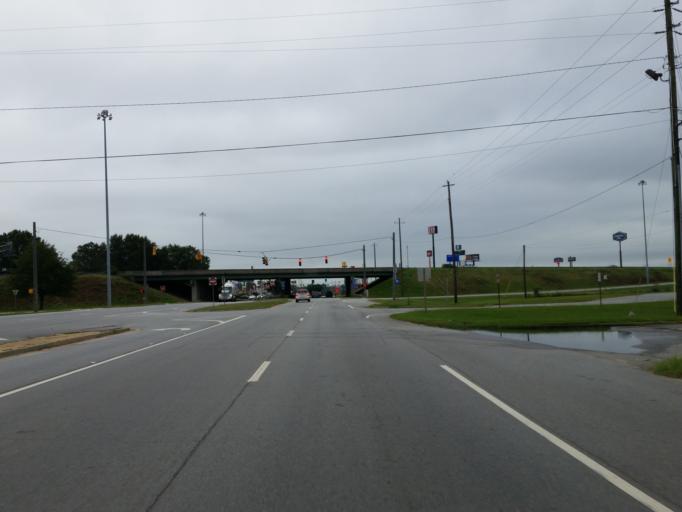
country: US
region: Georgia
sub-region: Houston County
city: Perry
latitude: 32.4728
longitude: -83.7452
